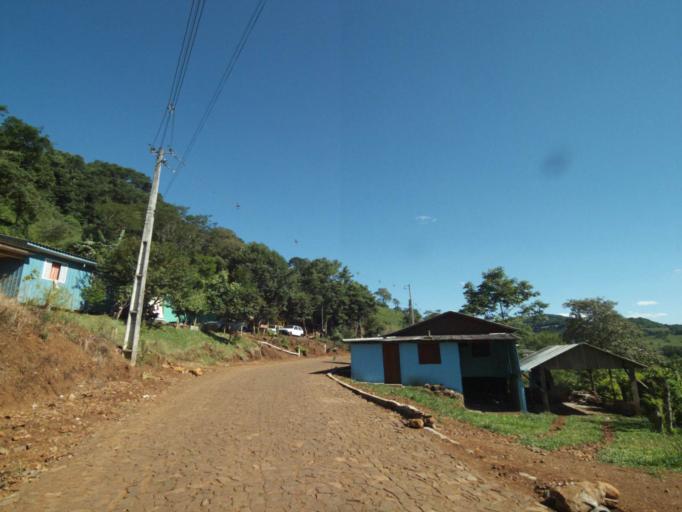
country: BR
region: Parana
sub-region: Ampere
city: Ampere
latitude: -26.1676
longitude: -53.3602
